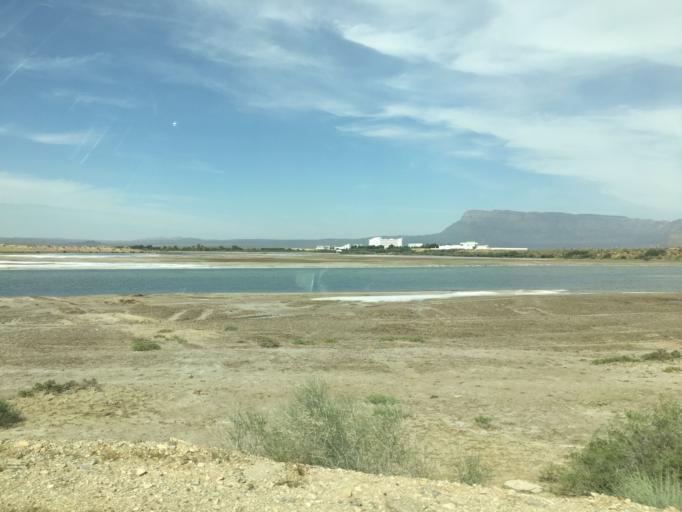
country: TM
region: Balkan
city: Balkanabat
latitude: 39.6211
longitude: 54.1627
